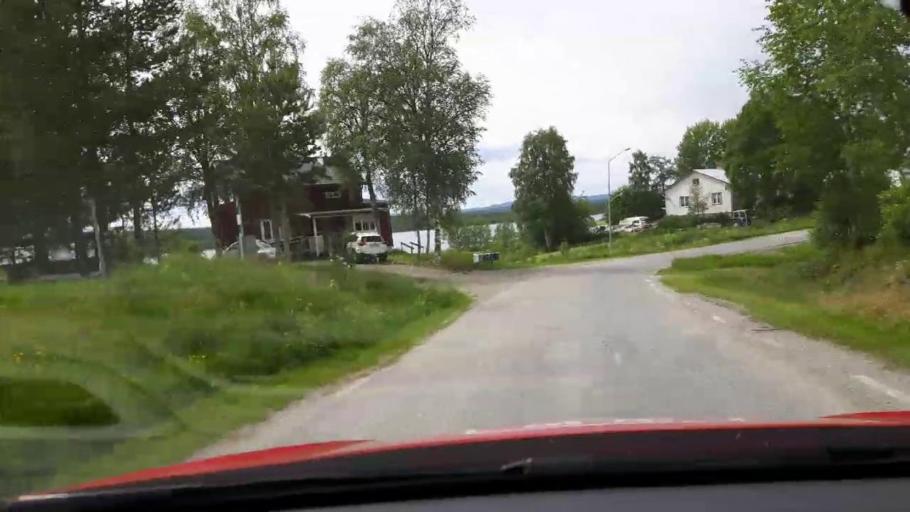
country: SE
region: Jaemtland
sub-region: Harjedalens Kommun
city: Sveg
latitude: 62.4067
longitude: 13.6947
